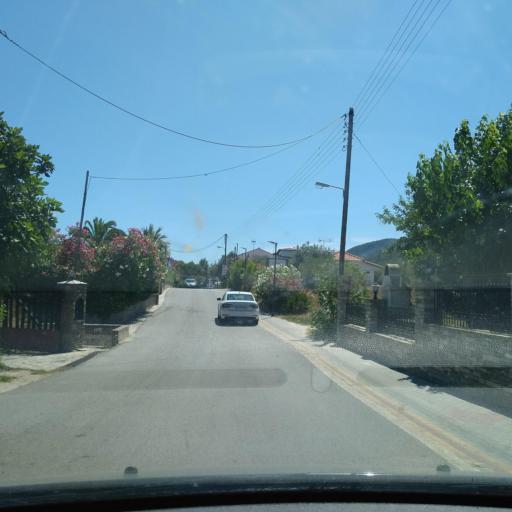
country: GR
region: Central Macedonia
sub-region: Nomos Chalkidikis
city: Neos Marmaras
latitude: 40.1875
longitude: 23.7869
